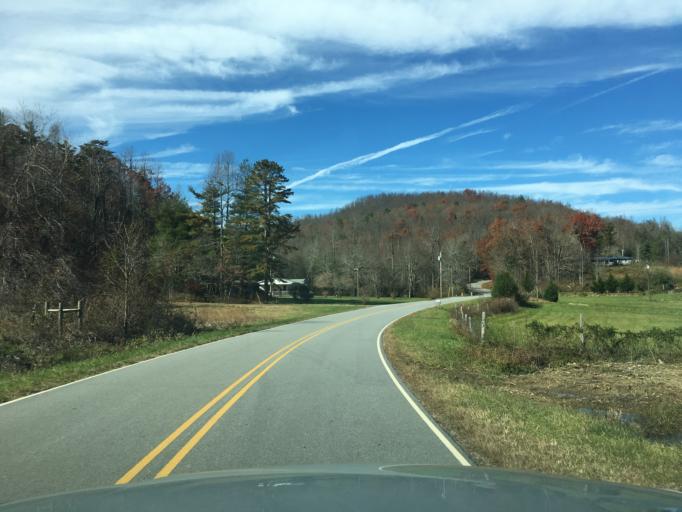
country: US
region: North Carolina
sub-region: Henderson County
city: Flat Rock
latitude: 35.2175
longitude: -82.4946
